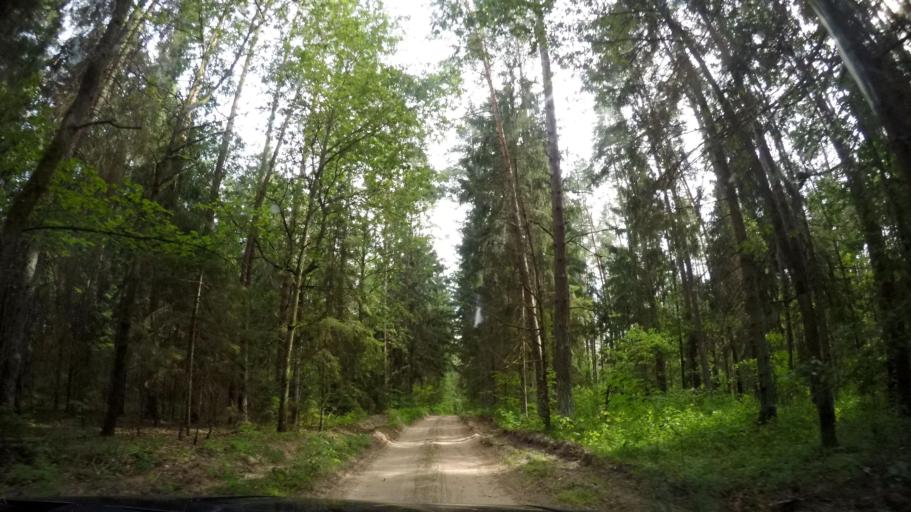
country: BY
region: Grodnenskaya
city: Skidal'
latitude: 53.8349
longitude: 24.1767
